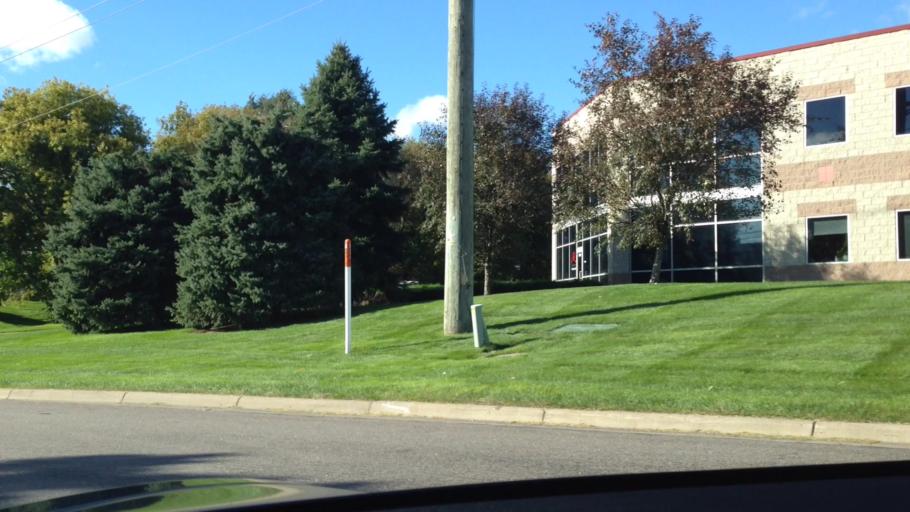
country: US
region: Minnesota
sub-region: Hennepin County
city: Osseo
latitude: 45.1161
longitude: -93.3869
